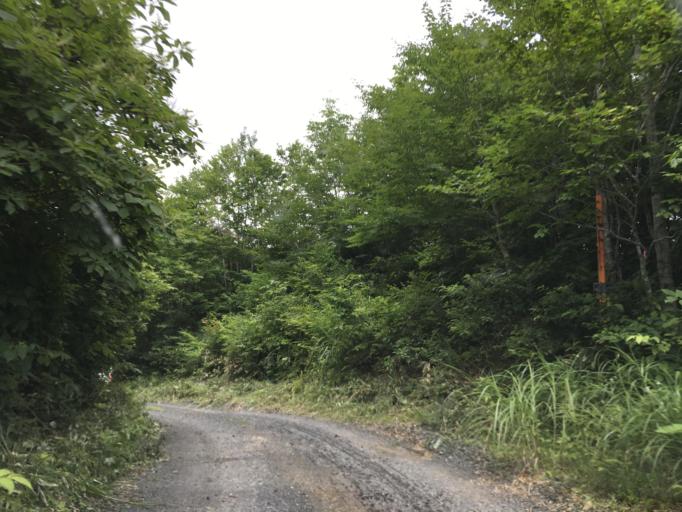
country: JP
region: Iwate
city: Ichinoseki
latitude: 38.9537
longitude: 140.8498
